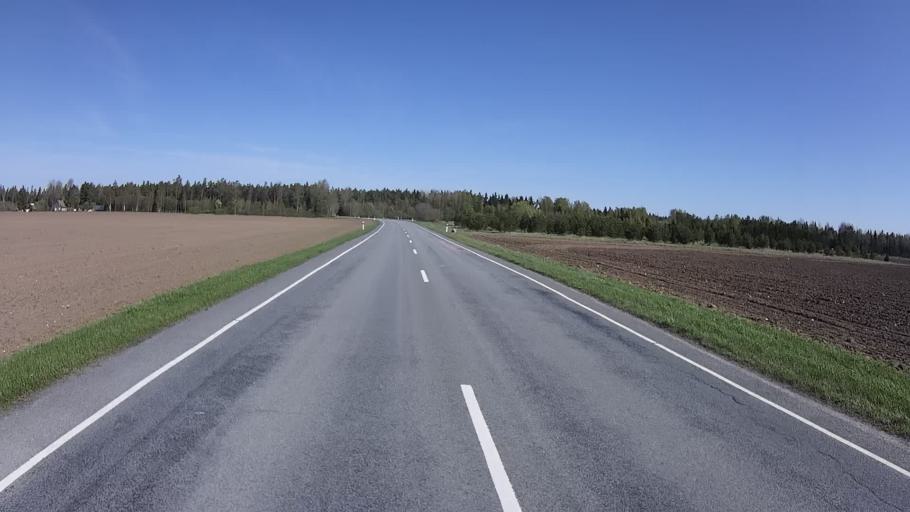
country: EE
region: Raplamaa
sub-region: Jaervakandi vald
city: Jarvakandi
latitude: 58.8467
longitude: 24.7960
